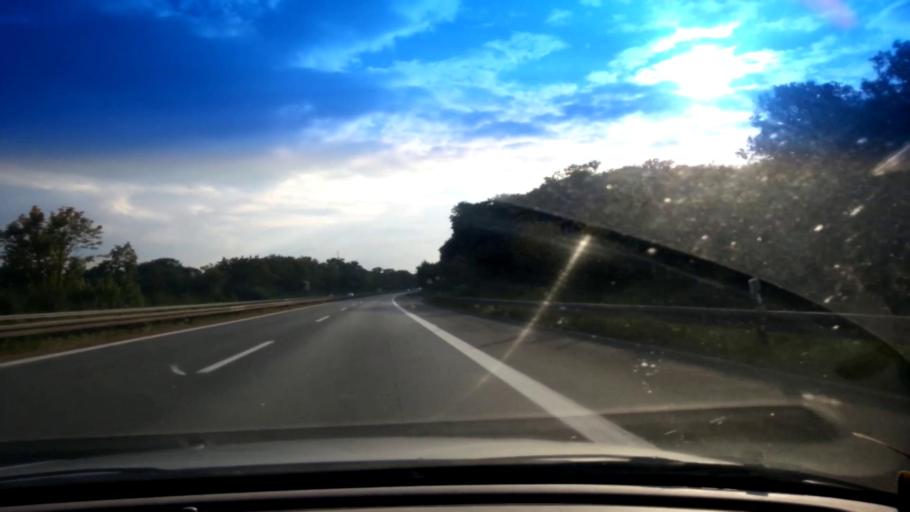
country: DE
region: Bavaria
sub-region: Upper Franconia
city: Schesslitz
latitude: 49.9734
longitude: 11.0154
